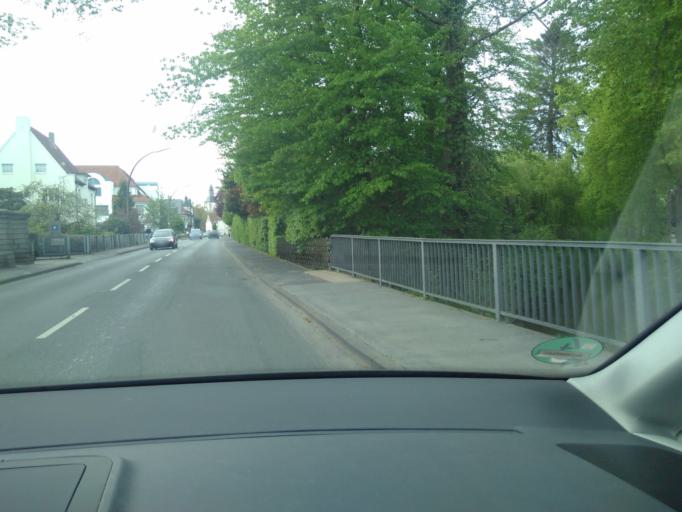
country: DE
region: North Rhine-Westphalia
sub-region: Regierungsbezirk Detmold
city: Rheda-Wiedenbruck
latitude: 51.8337
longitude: 8.3186
